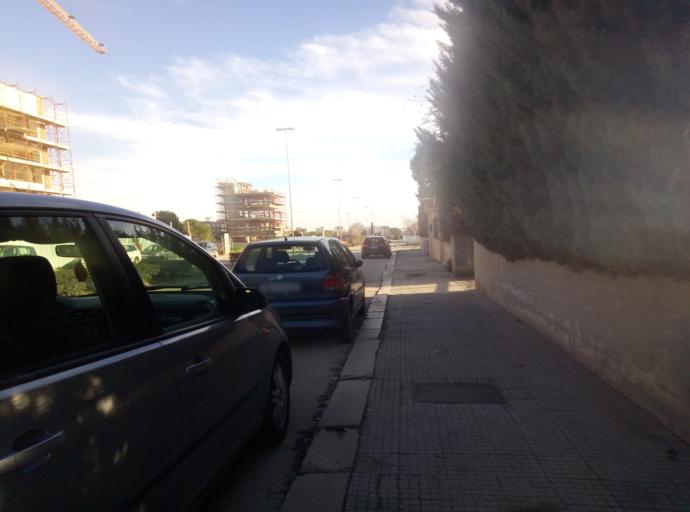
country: IT
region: Apulia
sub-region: Provincia di Bari
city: Ruvo di Puglia
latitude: 41.1203
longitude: 16.4911
